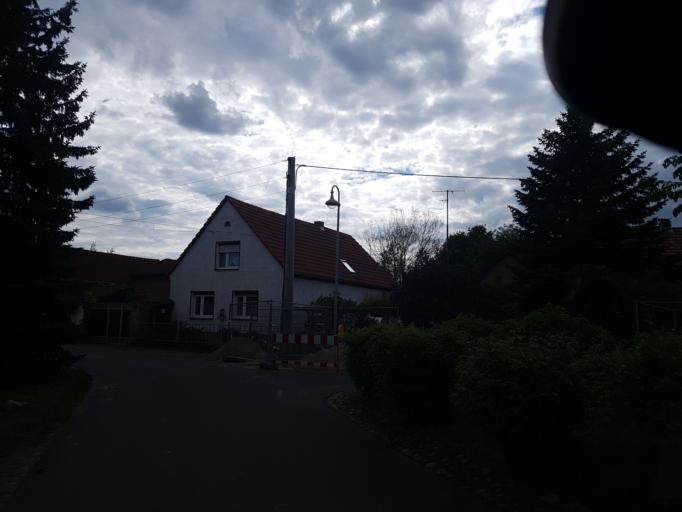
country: DE
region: Brandenburg
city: Grossraschen
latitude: 51.5877
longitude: 14.0599
